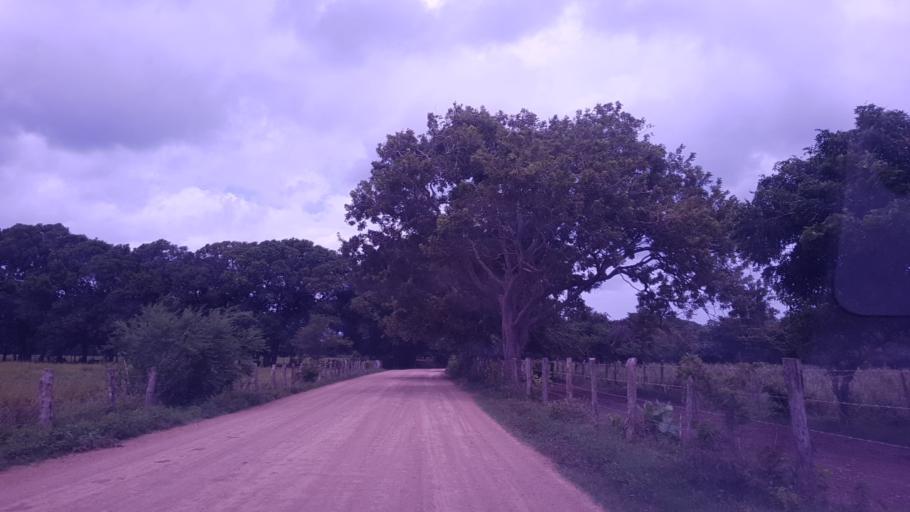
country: NI
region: Rivas
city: Tola
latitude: 11.4587
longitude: -86.0871
